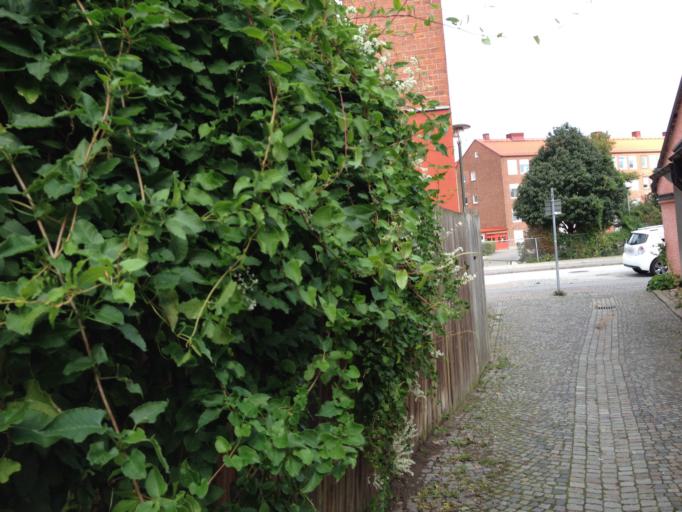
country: SE
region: Skane
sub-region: Malmo
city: Malmoe
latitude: 55.6106
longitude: 13.0371
